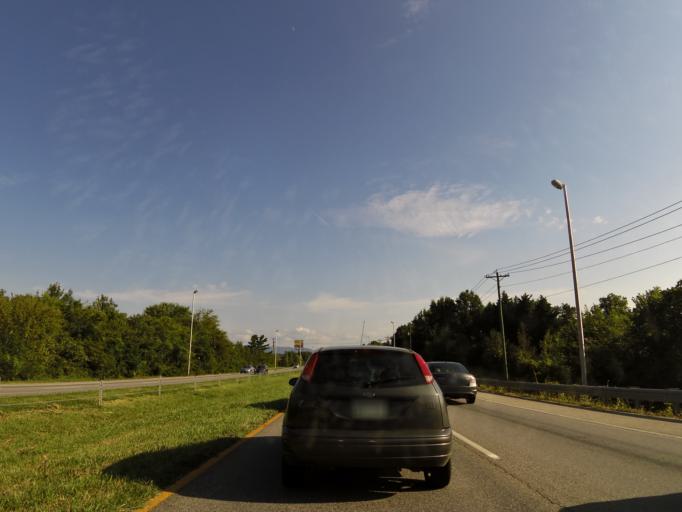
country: US
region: Tennessee
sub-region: Blount County
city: Alcoa
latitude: 35.7792
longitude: -83.9901
